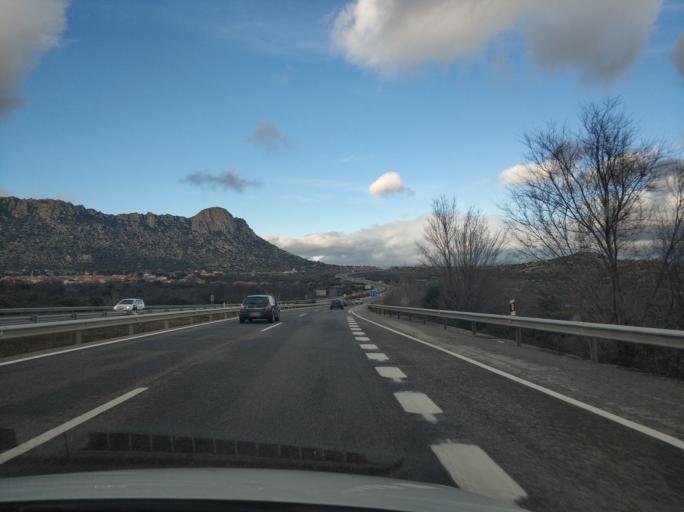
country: ES
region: Madrid
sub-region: Provincia de Madrid
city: La Cabrera
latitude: 40.8572
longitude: -3.6100
